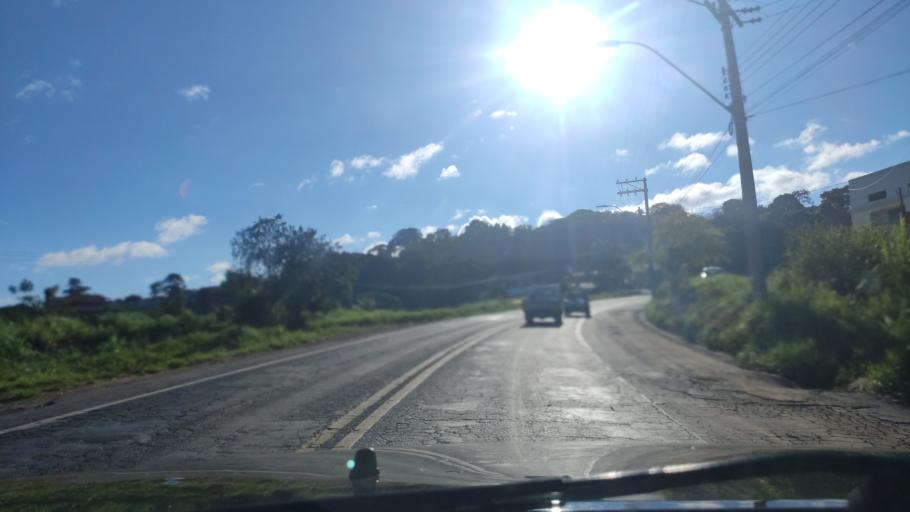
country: BR
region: Sao Paulo
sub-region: Socorro
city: Socorro
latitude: -22.5802
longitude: -46.5182
